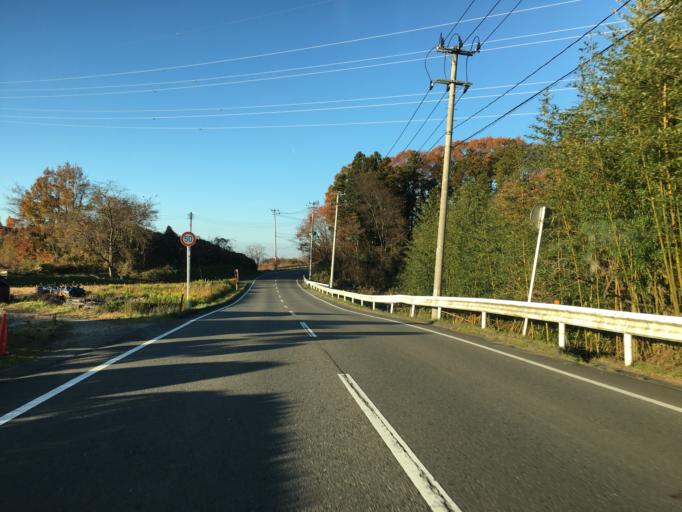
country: JP
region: Fukushima
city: Miharu
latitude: 37.3942
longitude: 140.4425
